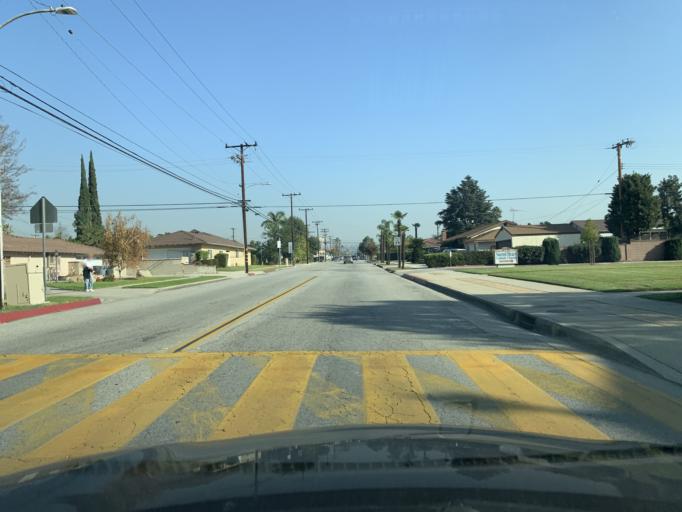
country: US
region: California
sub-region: Los Angeles County
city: Covina
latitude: 34.0754
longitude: -117.8950
